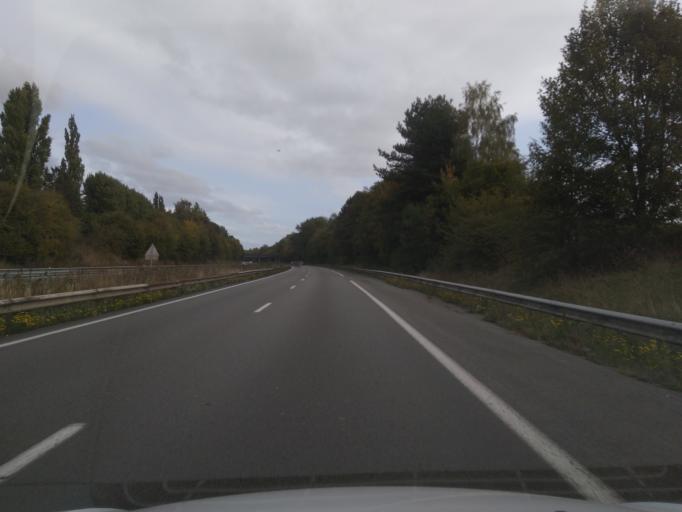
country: FR
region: Nord-Pas-de-Calais
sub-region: Departement du Nord
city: Marly
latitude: 50.3380
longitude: 3.5614
